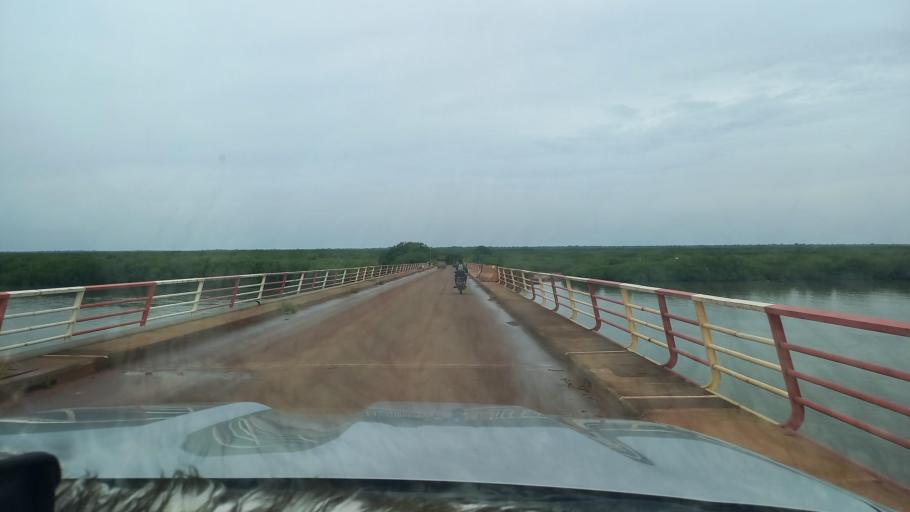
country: SN
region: Ziguinchor
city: Ziguinchor
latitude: 12.5906
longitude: -16.2626
